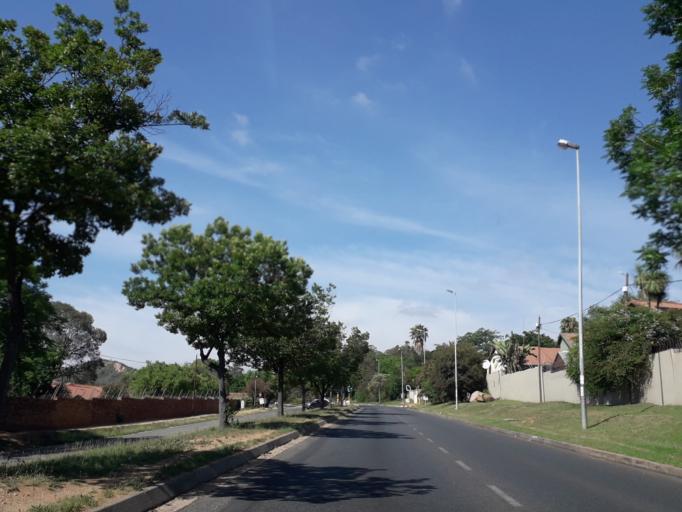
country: ZA
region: Gauteng
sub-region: City of Johannesburg Metropolitan Municipality
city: Roodepoort
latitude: -26.0750
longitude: 27.9611
